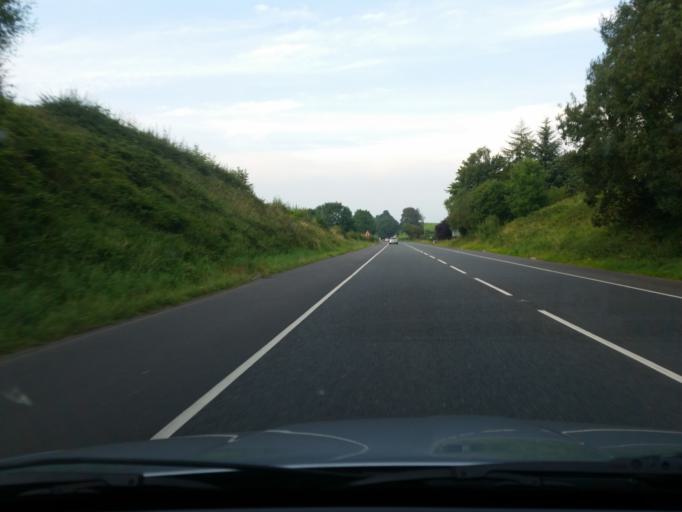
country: GB
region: Northern Ireland
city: Lisnaskea
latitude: 54.3194
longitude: -7.4050
